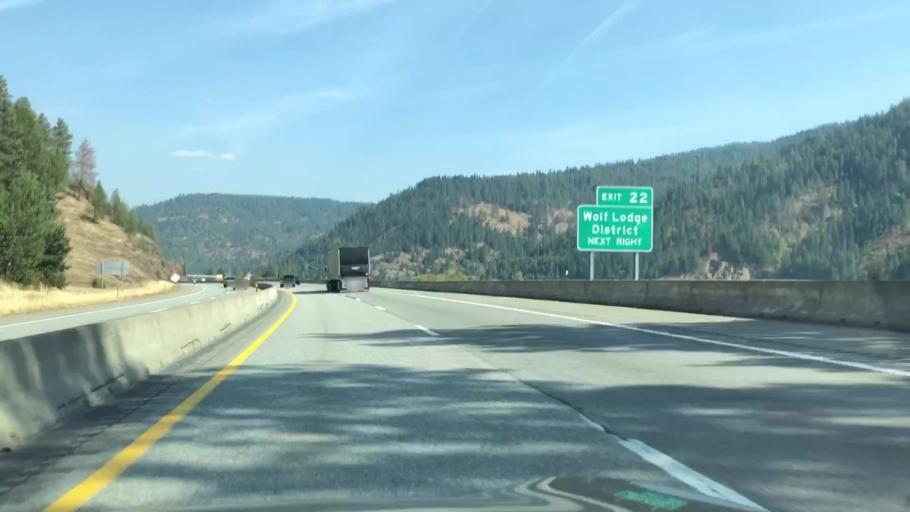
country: US
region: Idaho
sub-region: Kootenai County
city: Coeur d'Alene
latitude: 47.6236
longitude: -116.6634
